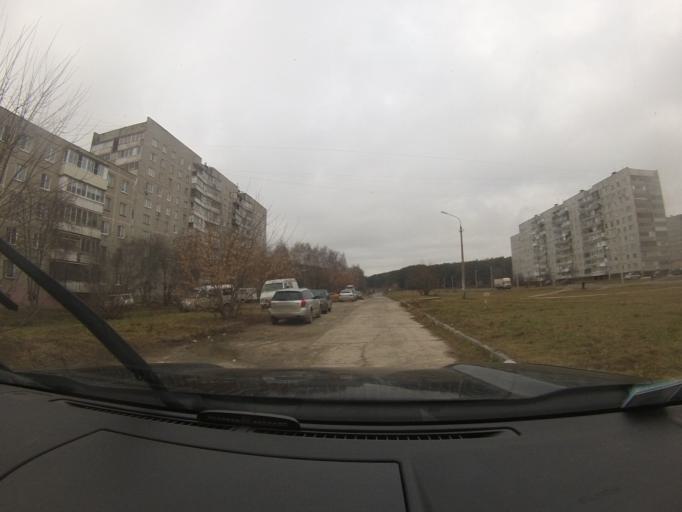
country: RU
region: Moskovskaya
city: Peski
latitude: 55.2742
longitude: 38.7532
